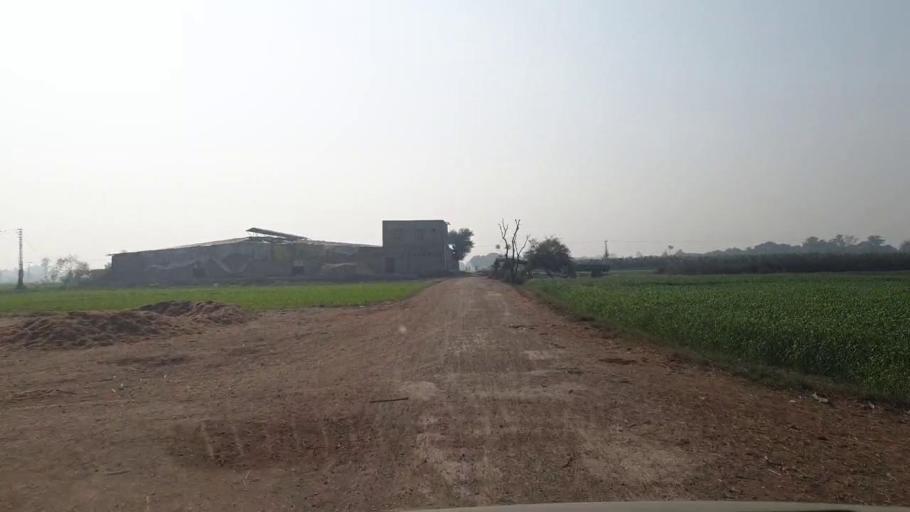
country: PK
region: Sindh
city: Sakrand
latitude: 25.9991
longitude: 68.3674
